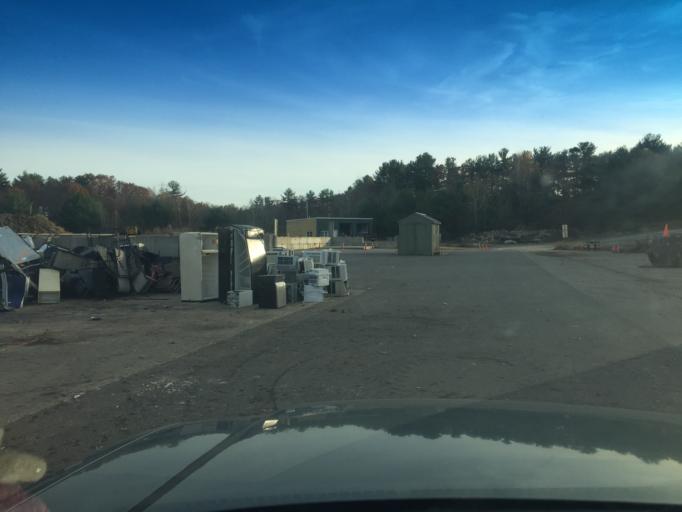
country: US
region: Maine
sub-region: York County
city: Eliot
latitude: 43.1984
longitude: -70.7452
